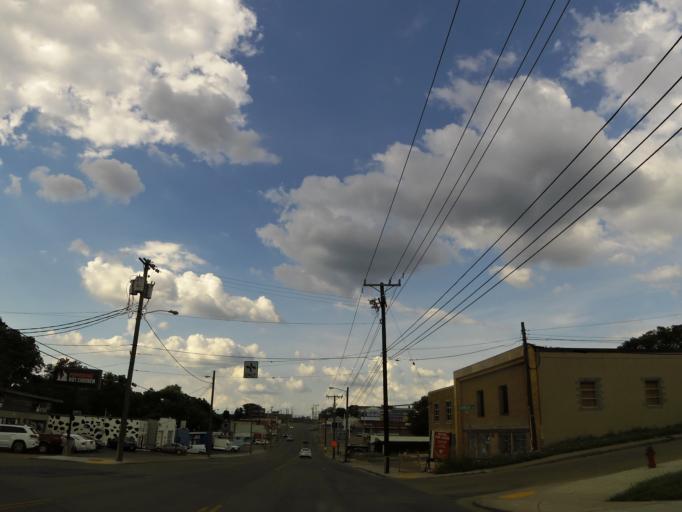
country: US
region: Tennessee
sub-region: Davidson County
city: Nashville
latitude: 36.1881
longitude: -86.7464
